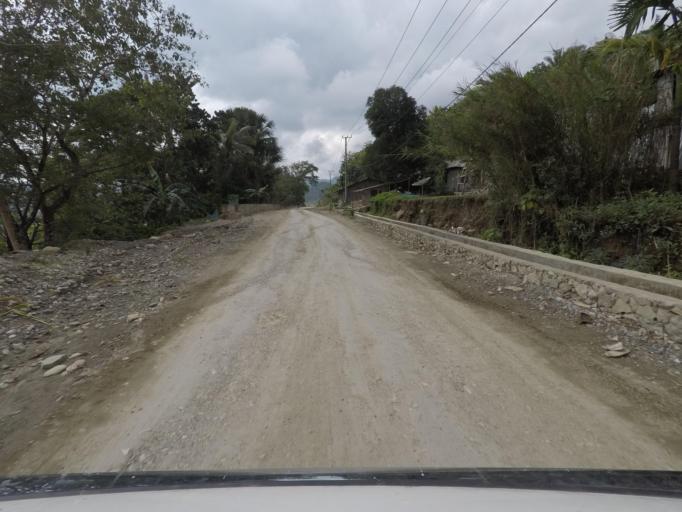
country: TL
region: Viqueque
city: Viqueque
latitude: -8.8301
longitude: 126.3737
